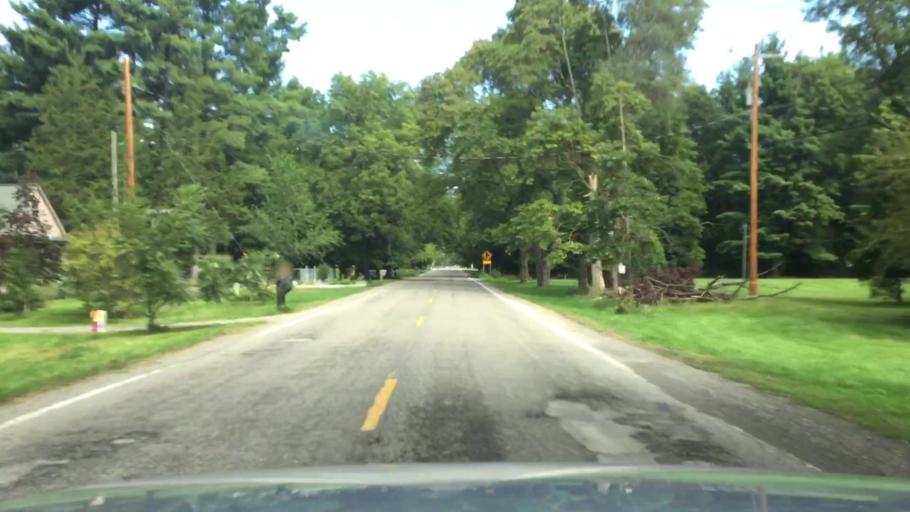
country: US
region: Michigan
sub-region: Wayne County
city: Belleville
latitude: 42.1538
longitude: -83.4612
